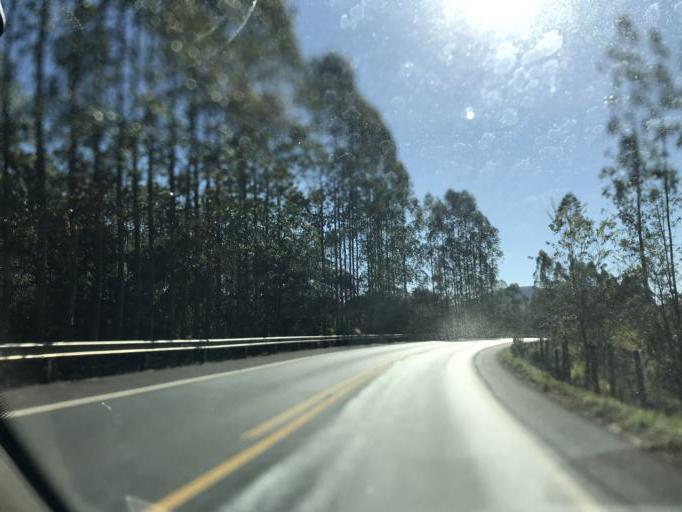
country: BR
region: Minas Gerais
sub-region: Bambui
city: Bambui
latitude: -19.8217
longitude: -46.0184
